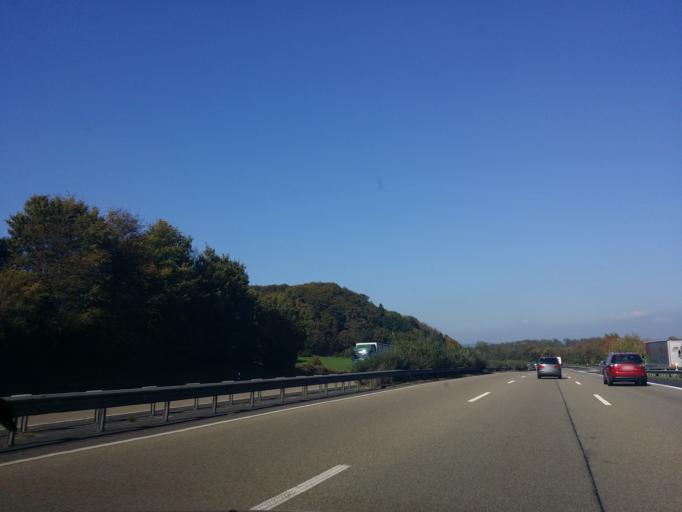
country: DE
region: Rheinland-Pfalz
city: Eppenrod
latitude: 50.4226
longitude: 7.9279
